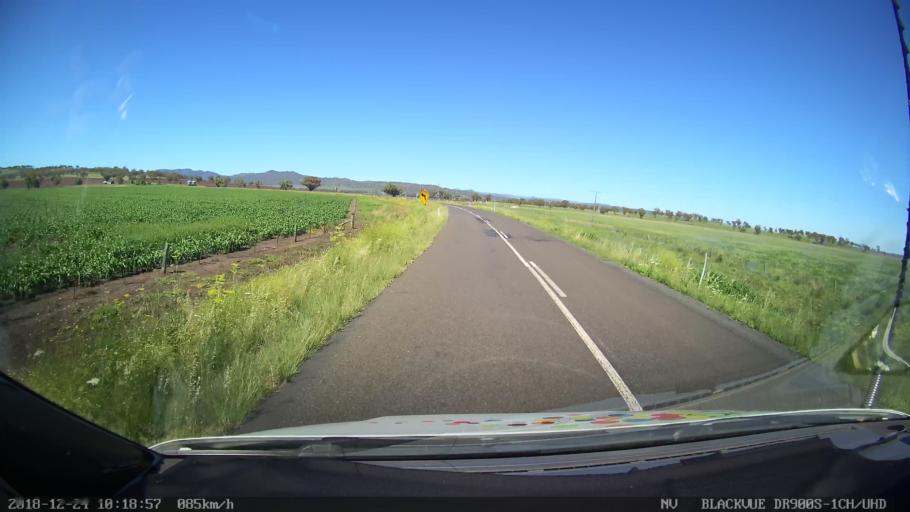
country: AU
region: New South Wales
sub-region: Liverpool Plains
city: Quirindi
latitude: -31.7259
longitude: 150.5688
